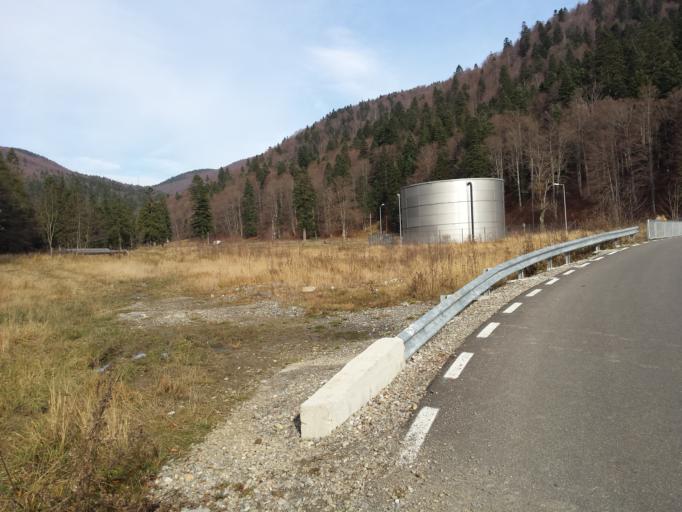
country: RO
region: Prahova
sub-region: Oras Azuga
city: Azuga
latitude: 45.4420
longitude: 25.5249
